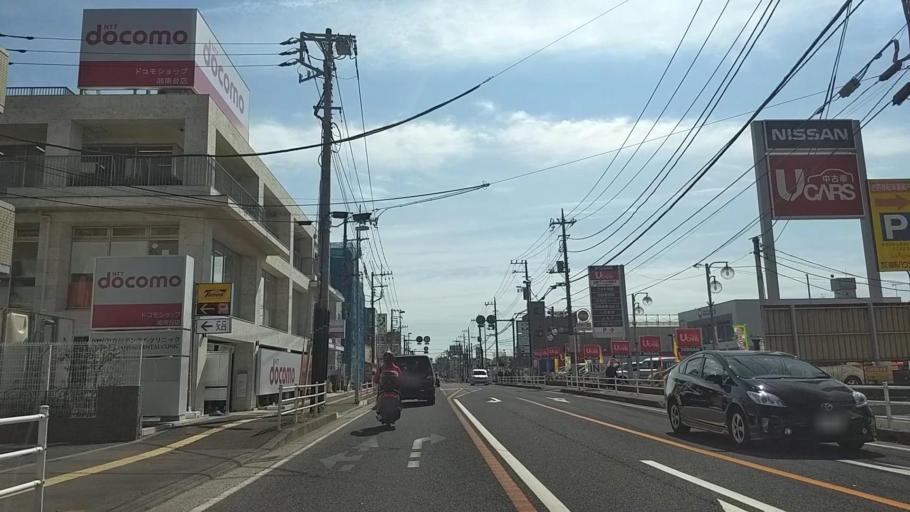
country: JP
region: Kanagawa
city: Fujisawa
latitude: 35.3961
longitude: 139.4707
